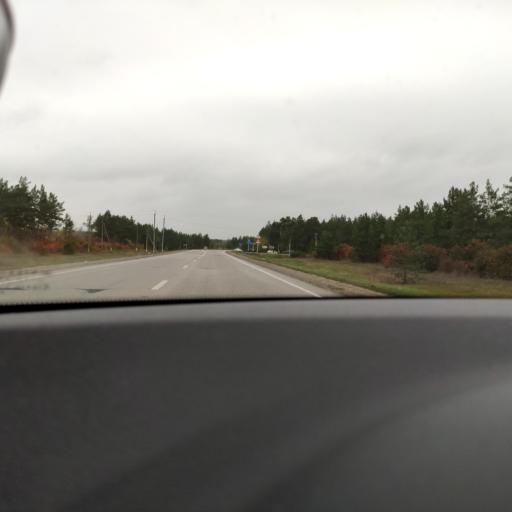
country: RU
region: Samara
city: Mirnyy
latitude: 53.5275
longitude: 50.3107
